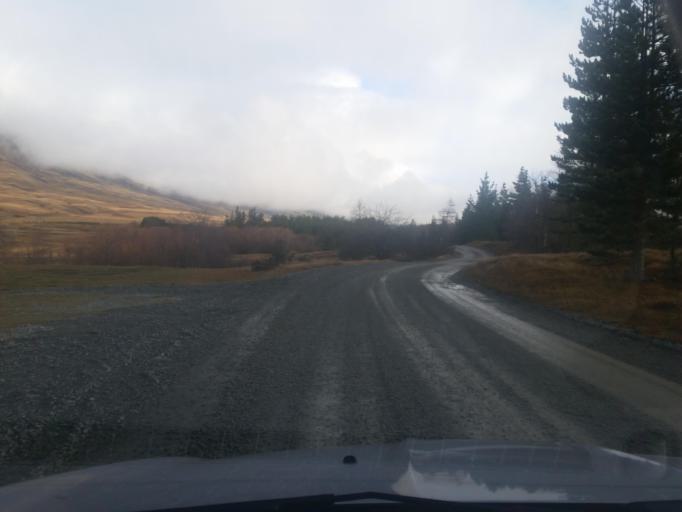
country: NZ
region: Canterbury
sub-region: Ashburton District
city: Methven
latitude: -43.6138
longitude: 171.0635
